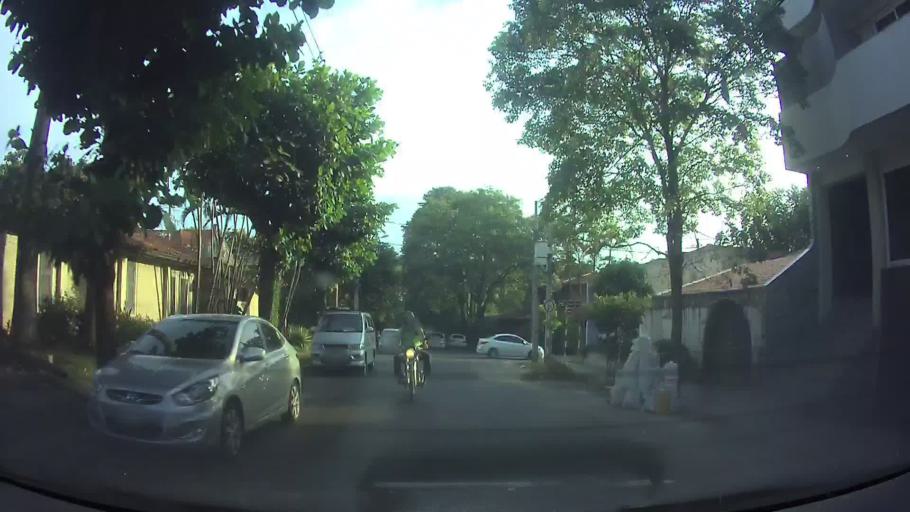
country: PY
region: Asuncion
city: Asuncion
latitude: -25.2792
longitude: -57.5740
